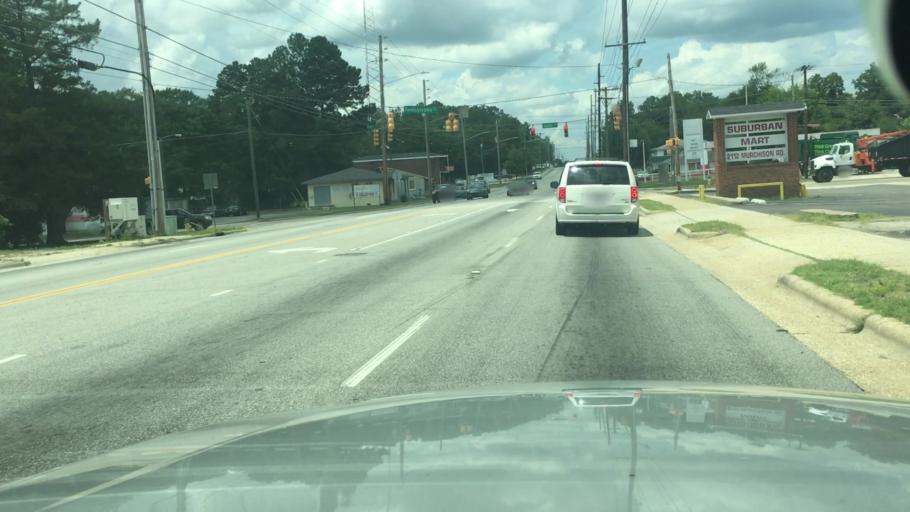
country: US
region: North Carolina
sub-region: Cumberland County
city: Fayetteville
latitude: 35.0842
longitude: -78.9044
